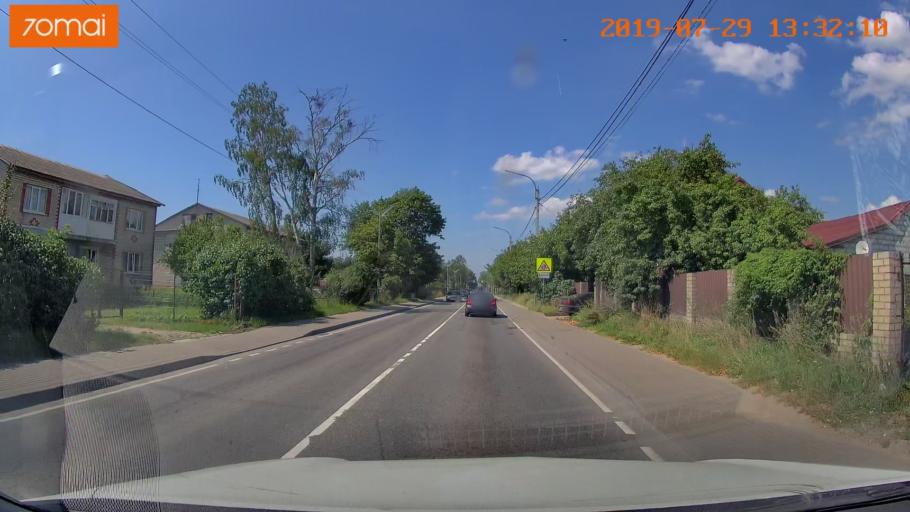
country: RU
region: Kaliningrad
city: Vzmorye
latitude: 54.6974
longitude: 20.2384
